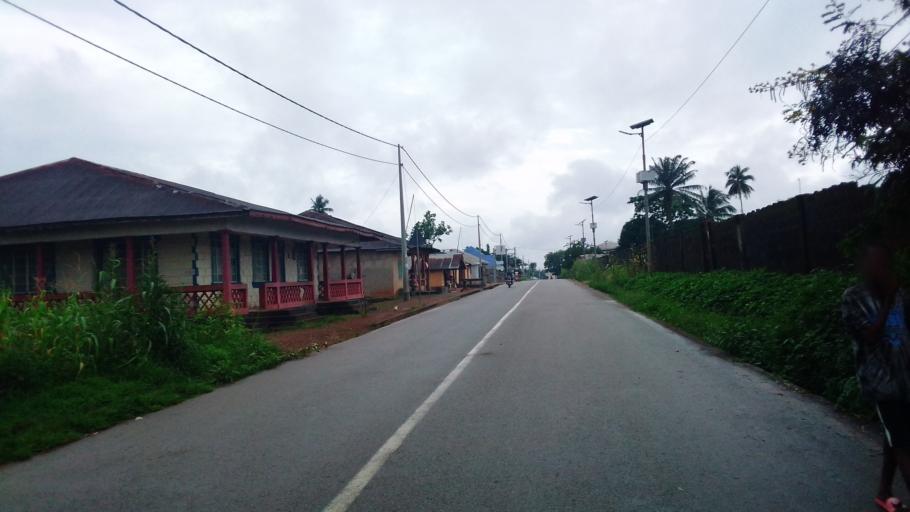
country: SL
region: Northern Province
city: Lunsar
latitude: 8.6850
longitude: -12.5292
